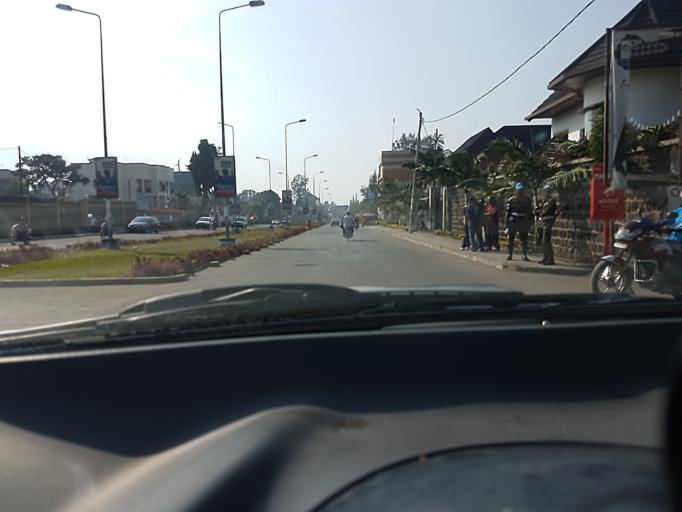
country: RW
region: Western Province
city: Gisenyi
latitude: -1.6931
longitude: 29.2388
